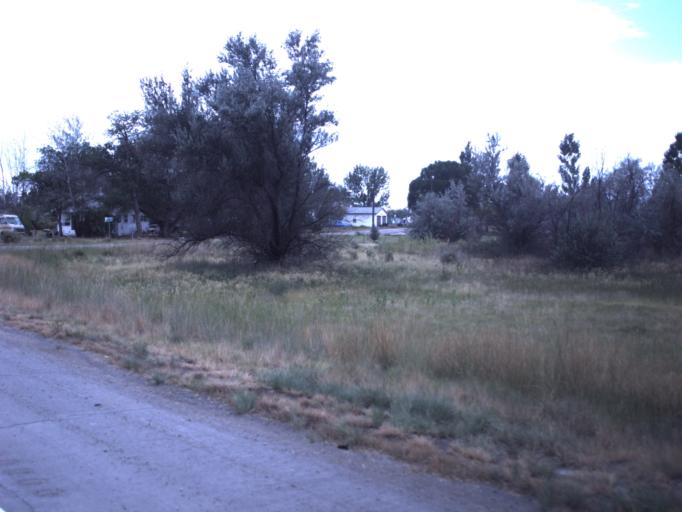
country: US
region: Utah
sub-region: Duchesne County
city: Roosevelt
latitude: 40.1973
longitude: -110.0692
